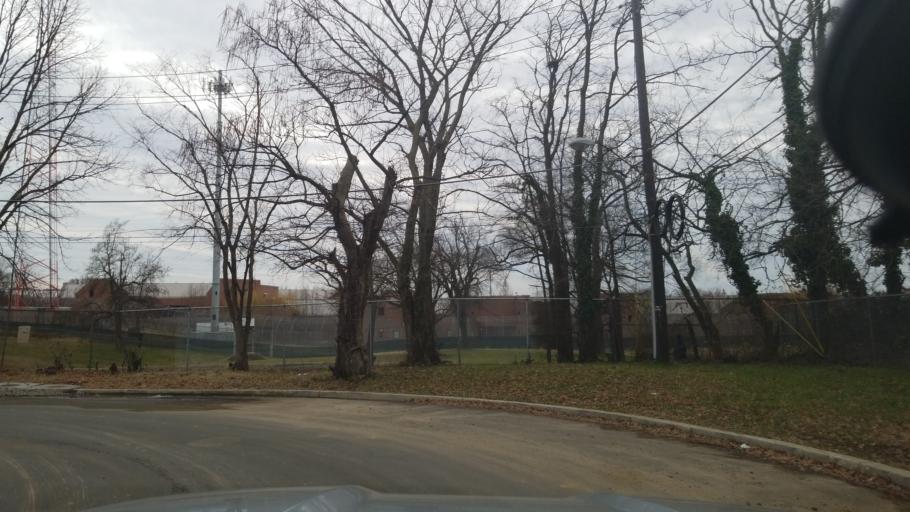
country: US
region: Maryland
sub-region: Prince George's County
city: Hillcrest Heights
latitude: 38.8500
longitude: -76.9863
